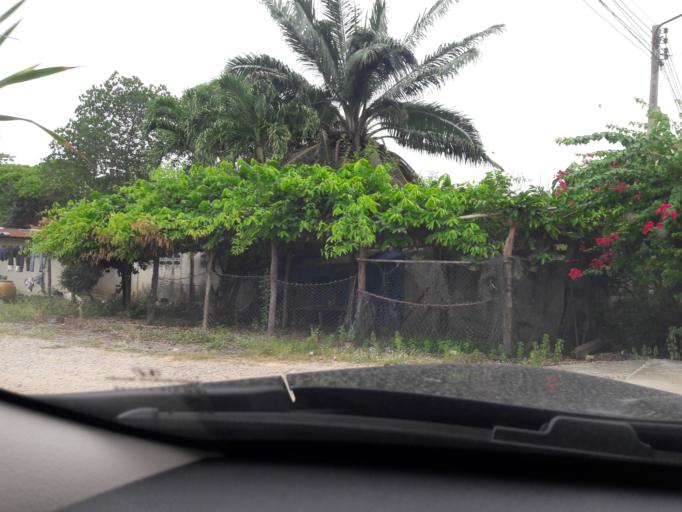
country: TH
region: Ratchaburi
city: Damnoen Saduak
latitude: 13.5974
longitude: 99.9074
